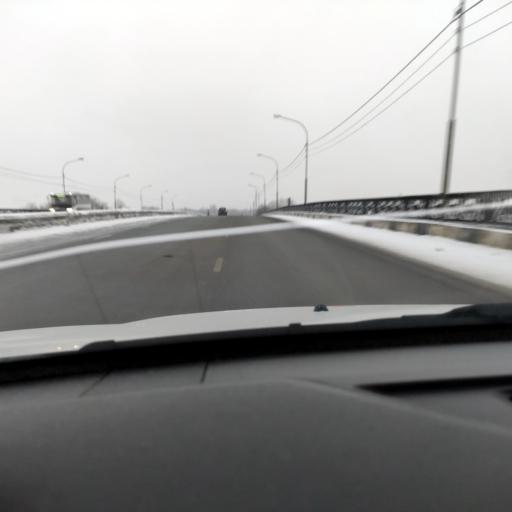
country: RU
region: Samara
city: Smyshlyayevka
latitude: 53.2539
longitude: 50.3666
